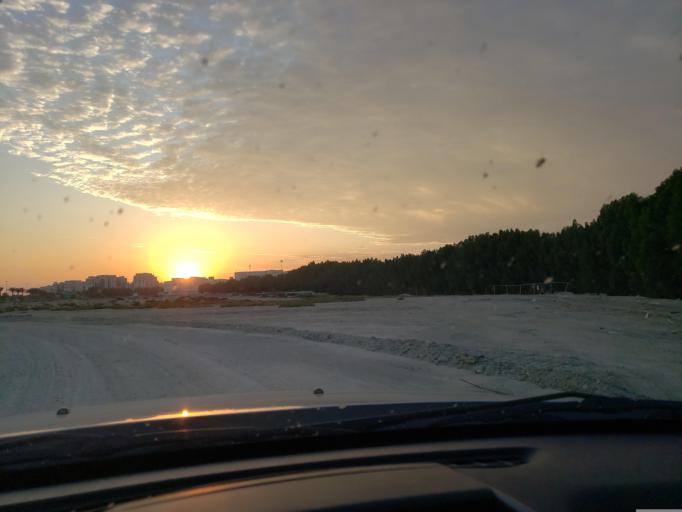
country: AE
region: Dubai
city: Dubai
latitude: 25.0113
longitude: 55.2597
